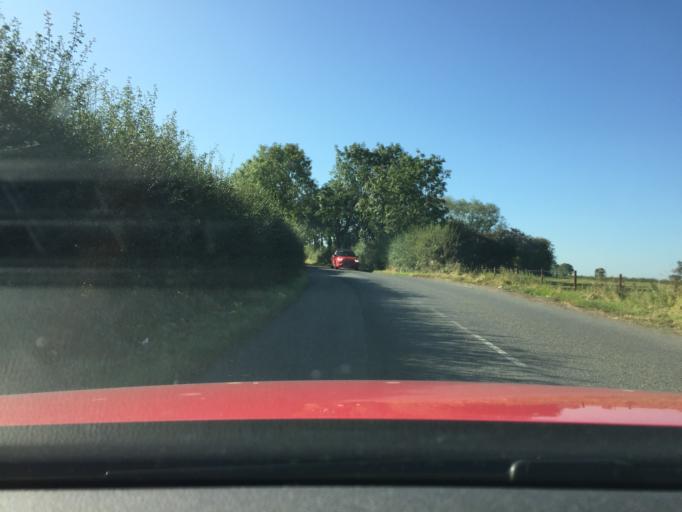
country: GB
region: England
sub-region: Leicestershire
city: Houghton on the Hill
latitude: 52.6650
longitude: -1.0225
